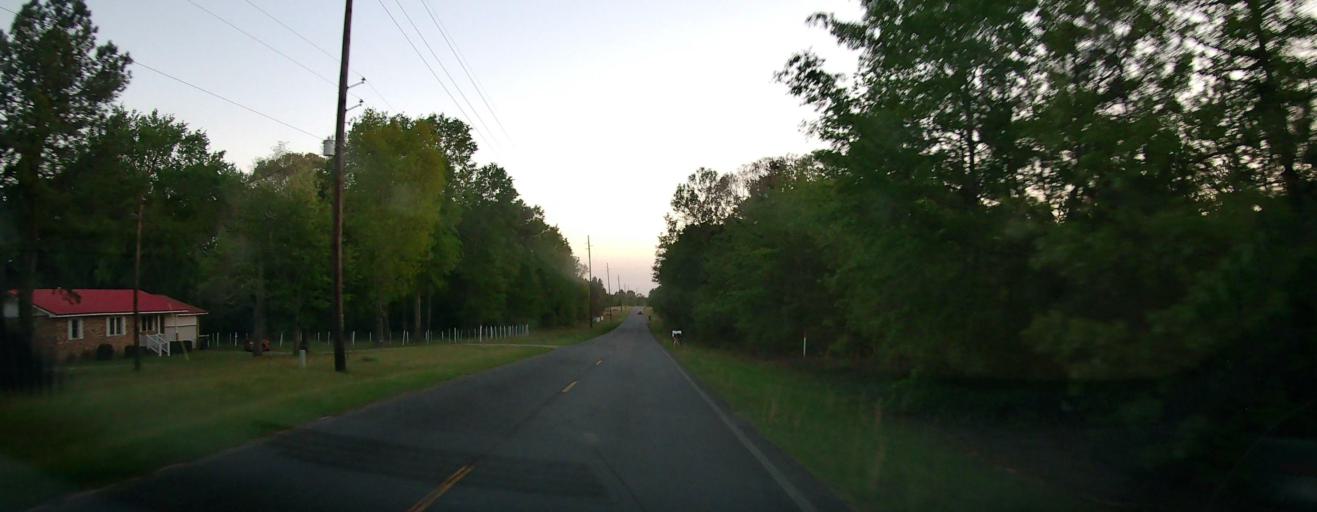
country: US
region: Georgia
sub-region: Marion County
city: Buena Vista
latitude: 32.2802
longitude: -84.5432
